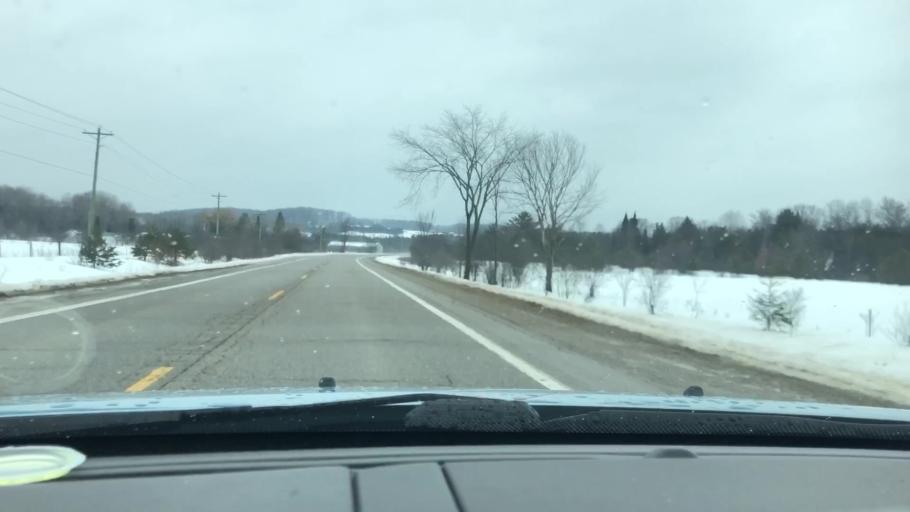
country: US
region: Michigan
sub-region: Charlevoix County
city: East Jordan
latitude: 45.1277
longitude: -85.1364
